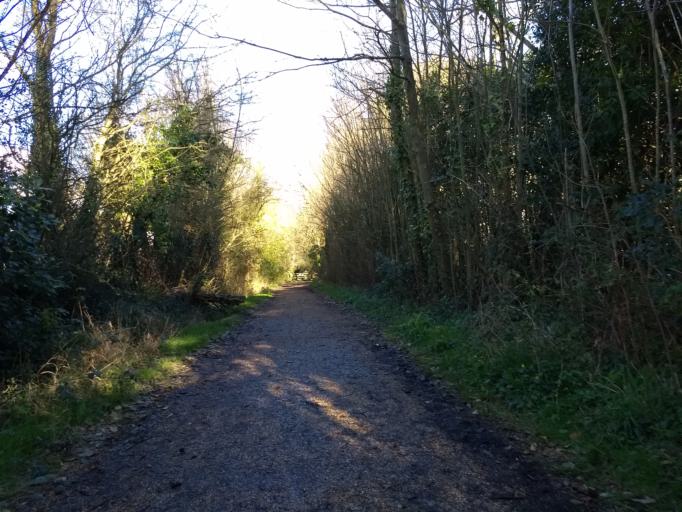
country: GB
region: England
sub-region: Isle of Wight
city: Ryde
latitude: 50.7311
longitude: -1.2095
